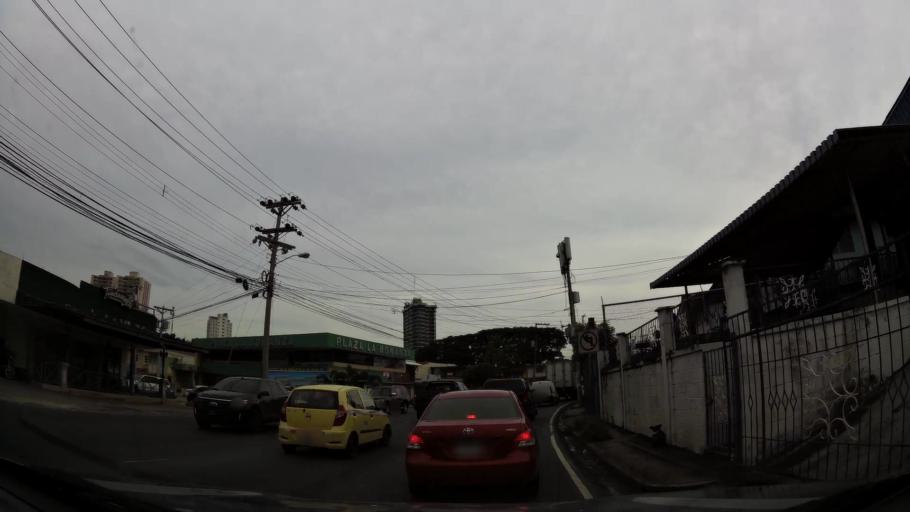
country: PA
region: Panama
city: Panama
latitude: 9.0193
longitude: -79.5227
